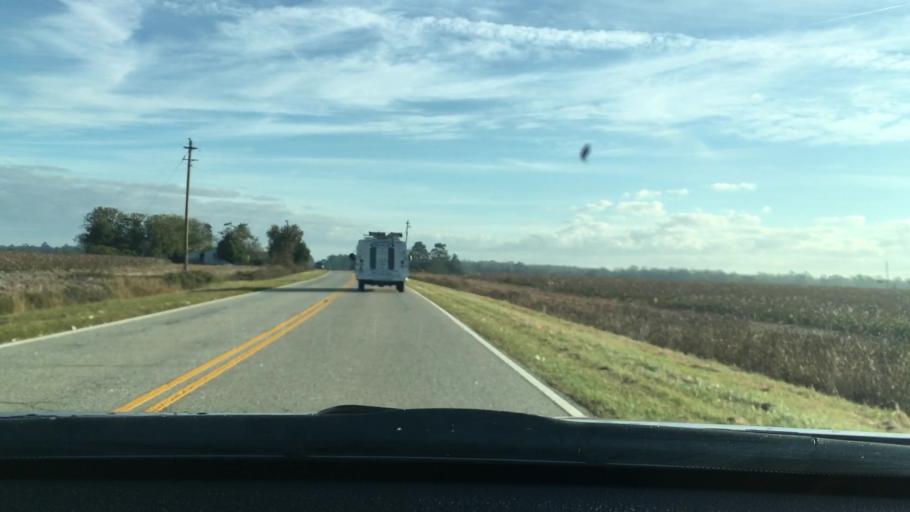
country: US
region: South Carolina
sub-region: Lee County
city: Bishopville
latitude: 34.0681
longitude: -80.2150
